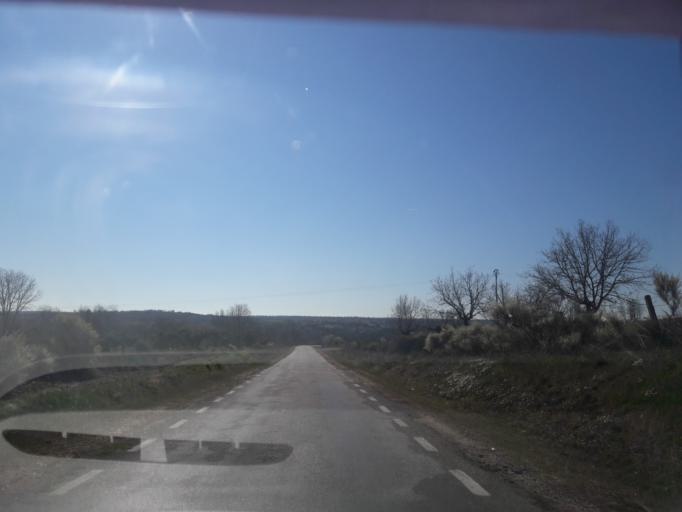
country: ES
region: Castille and Leon
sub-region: Provincia de Salamanca
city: Valsalabroso
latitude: 41.1648
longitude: -6.4993
